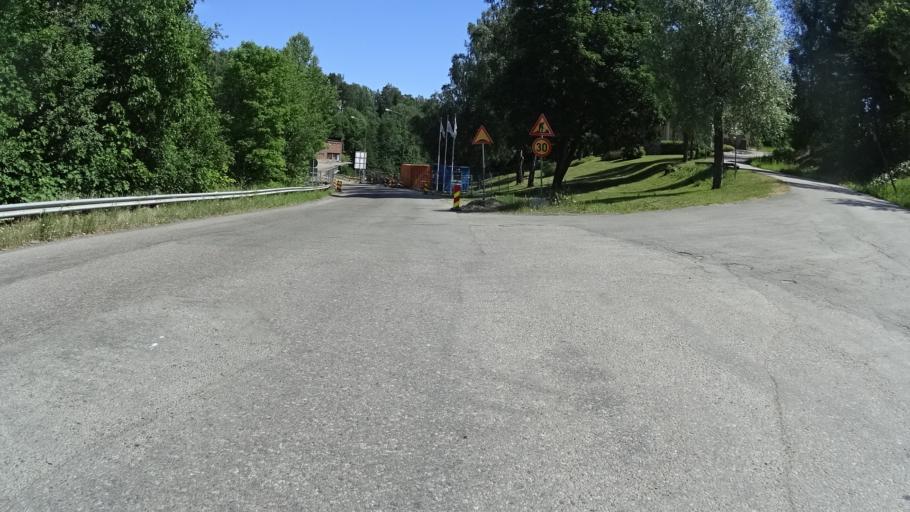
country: FI
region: Uusimaa
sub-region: Raaseporin
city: Pohja
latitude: 60.0949
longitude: 23.5885
